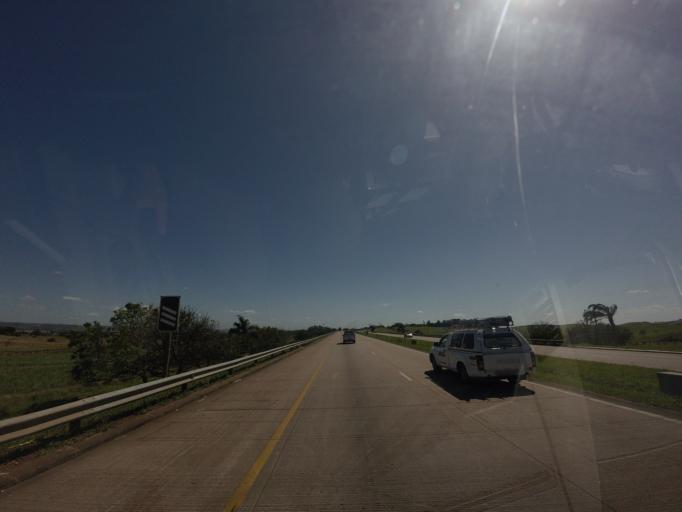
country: ZA
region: KwaZulu-Natal
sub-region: iLembe District Municipality
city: Stanger
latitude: -29.4136
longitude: 31.2785
